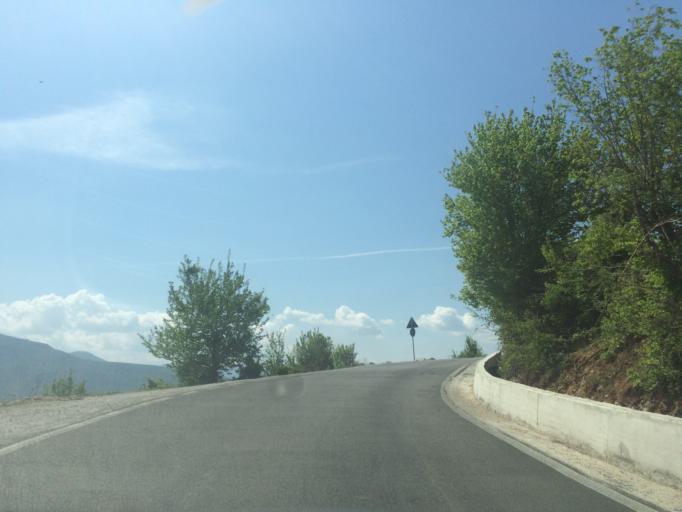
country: AL
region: Kukes
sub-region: Rrethi i Tropojes
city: Bajram Curri
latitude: 42.3574
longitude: 20.0934
